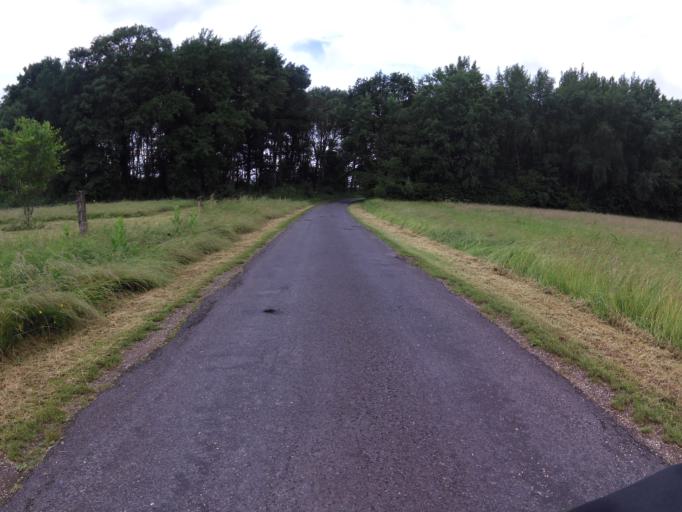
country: FR
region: Champagne-Ardenne
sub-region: Departement de la Marne
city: Sermaize-les-Bains
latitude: 48.7744
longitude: 4.9238
